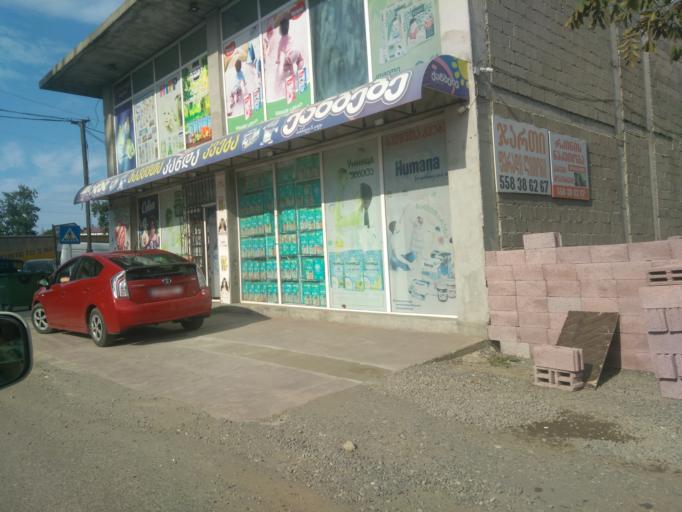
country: GE
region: Ajaria
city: Batumi
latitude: 41.6184
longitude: 41.6182
